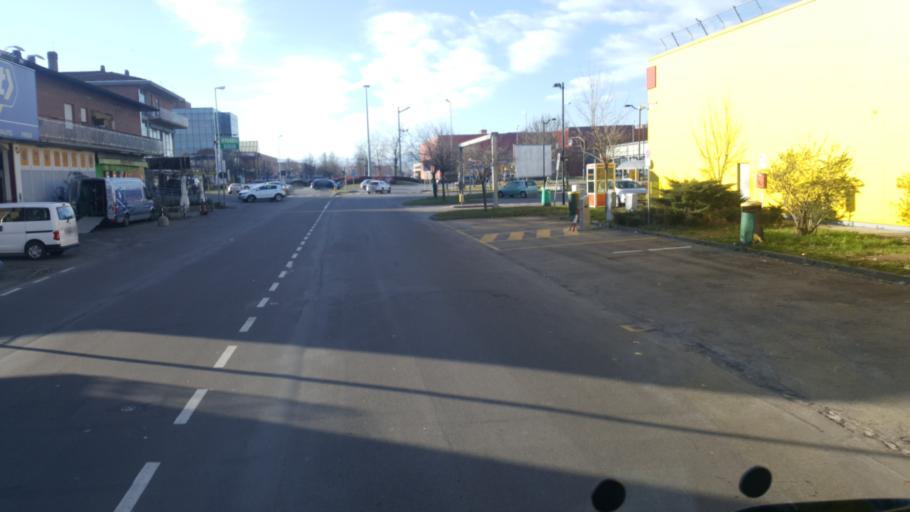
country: IT
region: Emilia-Romagna
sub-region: Provincia di Reggio Emilia
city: Rubiera
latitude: 44.6557
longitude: 10.7738
